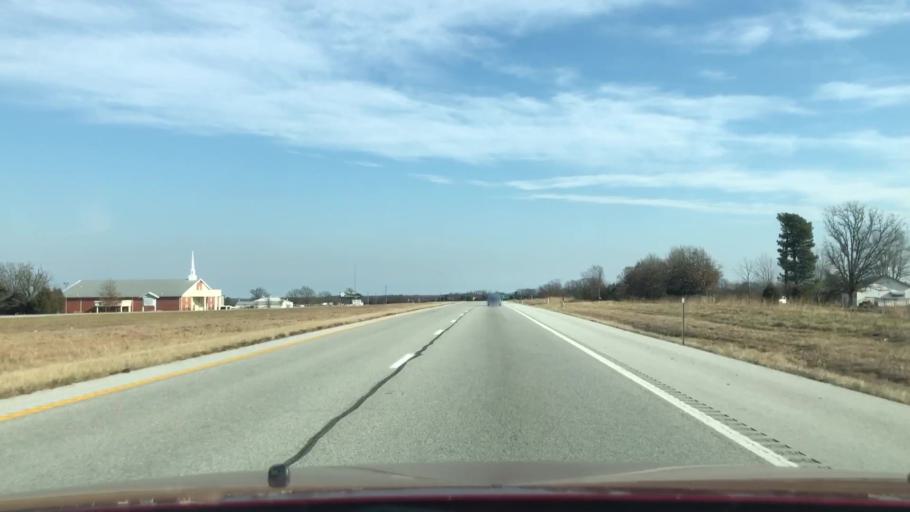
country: US
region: Missouri
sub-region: Webster County
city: Seymour
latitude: 37.1682
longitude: -92.8696
